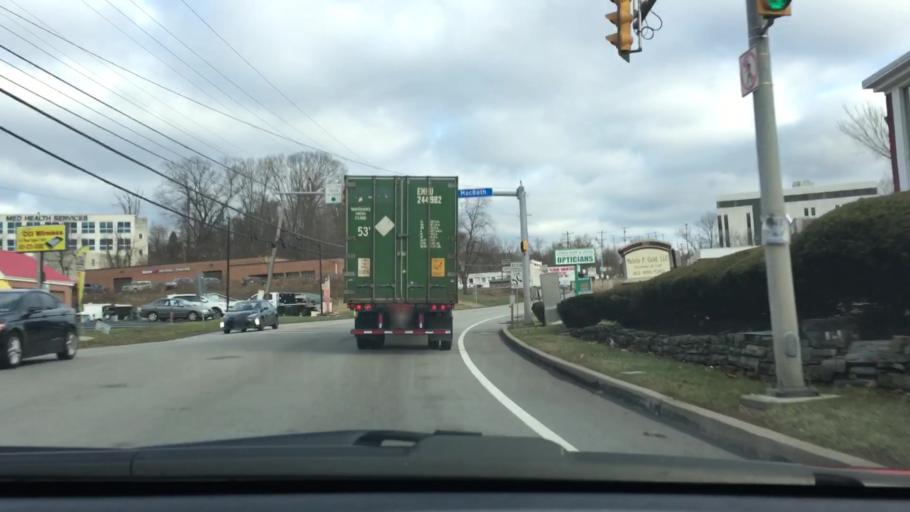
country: US
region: Pennsylvania
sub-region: Allegheny County
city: Pitcairn
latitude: 40.4254
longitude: -79.7544
